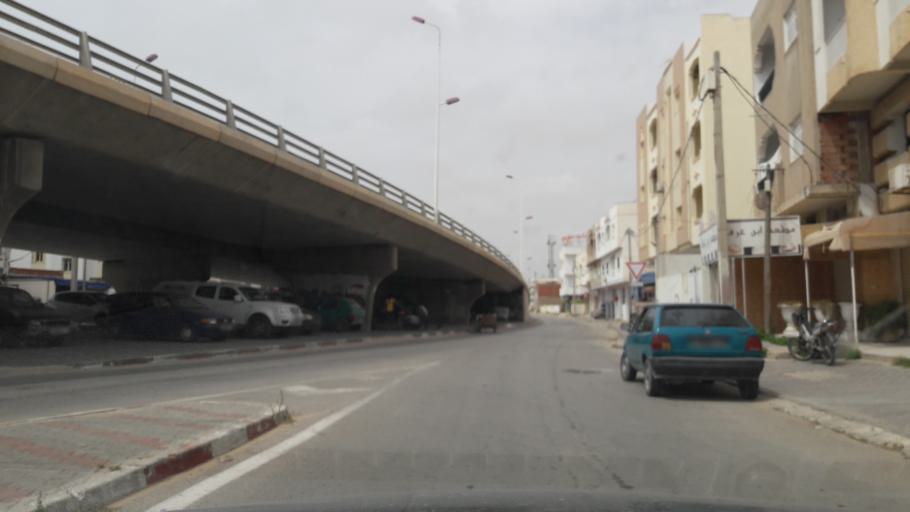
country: TN
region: Safaqis
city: Sfax
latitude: 34.7725
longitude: 10.7602
